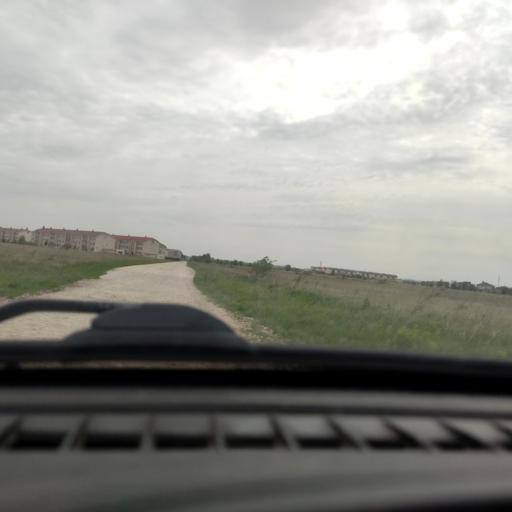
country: RU
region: Samara
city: Podstepki
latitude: 53.5282
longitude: 49.1719
